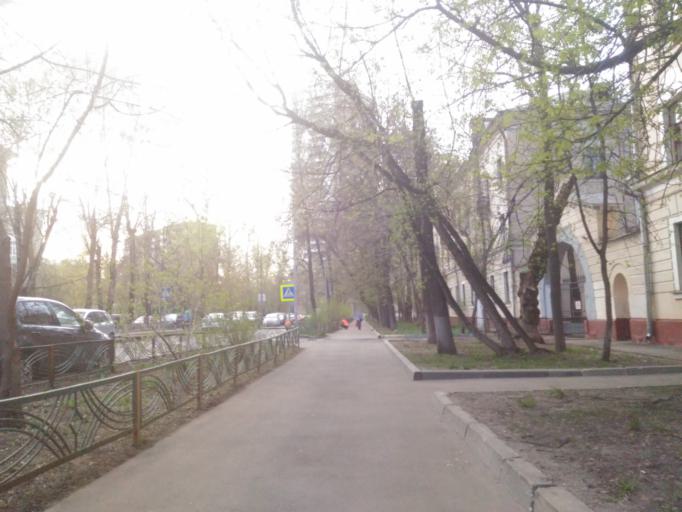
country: RU
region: Moskovskaya
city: Khoroshevo-Mnevniki
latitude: 55.7944
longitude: 37.4886
